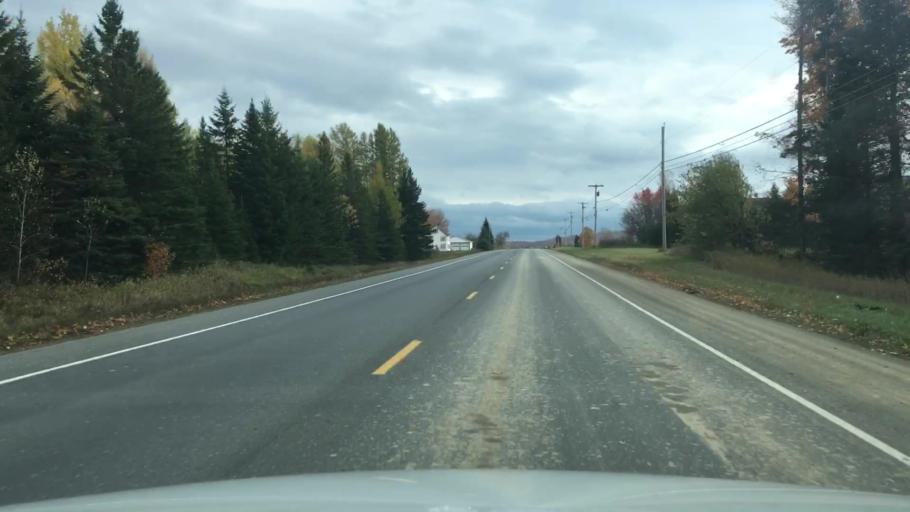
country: US
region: Maine
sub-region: Aroostook County
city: Easton
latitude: 46.5602
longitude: -67.9432
